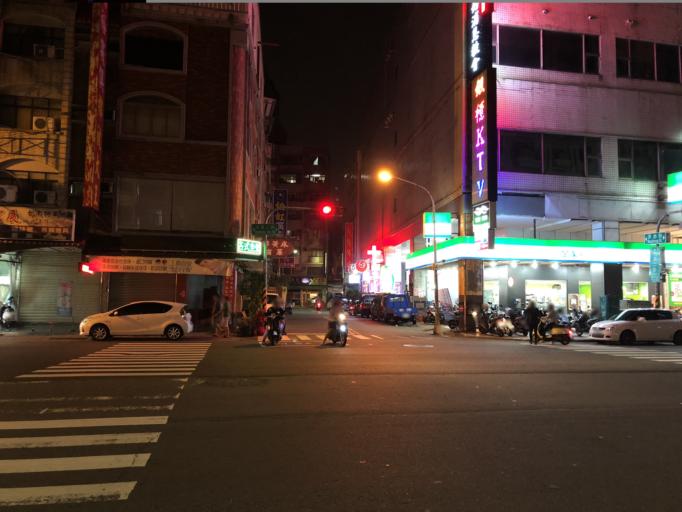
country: TW
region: Kaohsiung
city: Kaohsiung
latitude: 22.6420
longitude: 120.3322
